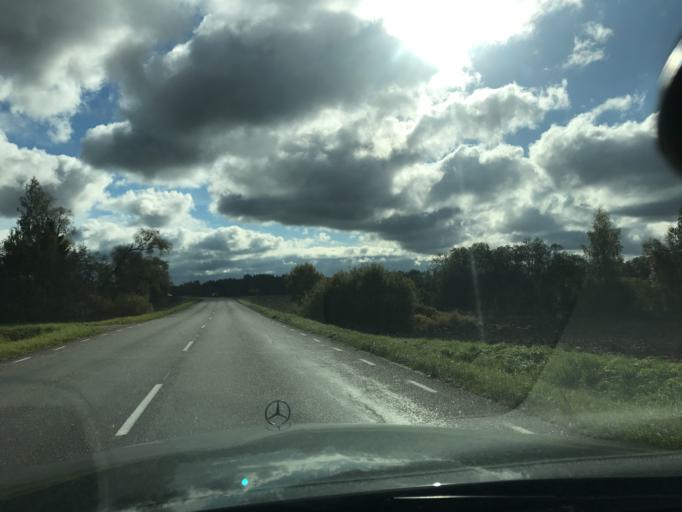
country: EE
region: Vorumaa
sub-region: Antsla vald
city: Vana-Antsla
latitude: 57.9086
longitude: 26.4198
